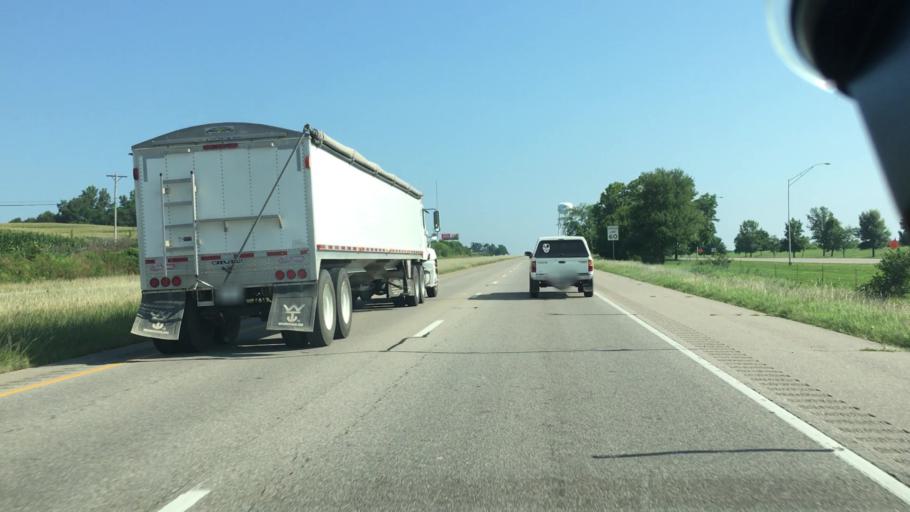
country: US
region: Indiana
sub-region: Gibson County
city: Fort Branch
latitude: 38.2830
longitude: -87.5675
